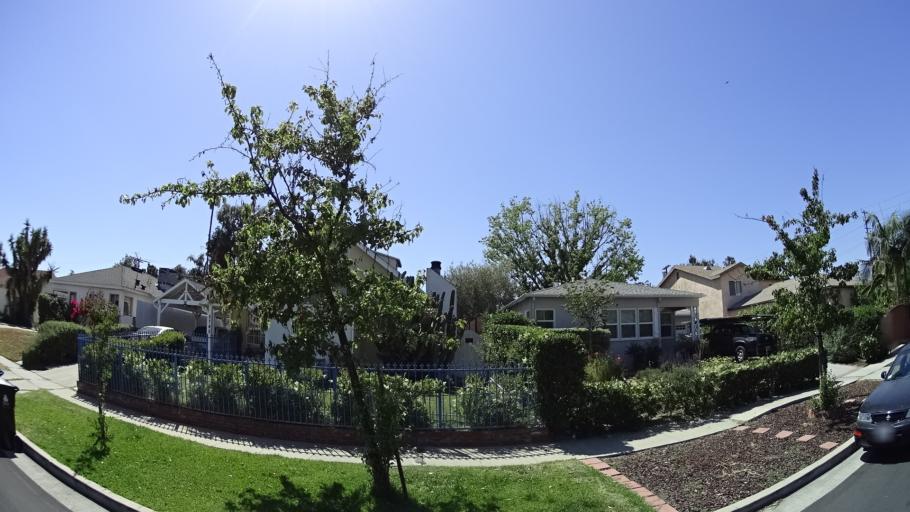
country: US
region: California
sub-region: Los Angeles County
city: North Hollywood
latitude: 34.1753
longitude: -118.3867
